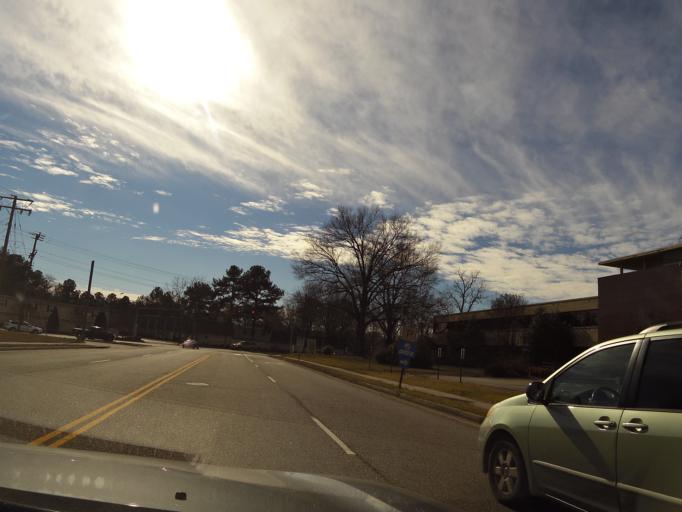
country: US
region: Virginia
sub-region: City of Hopewell
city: Hopewell
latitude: 37.2936
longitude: -77.2901
